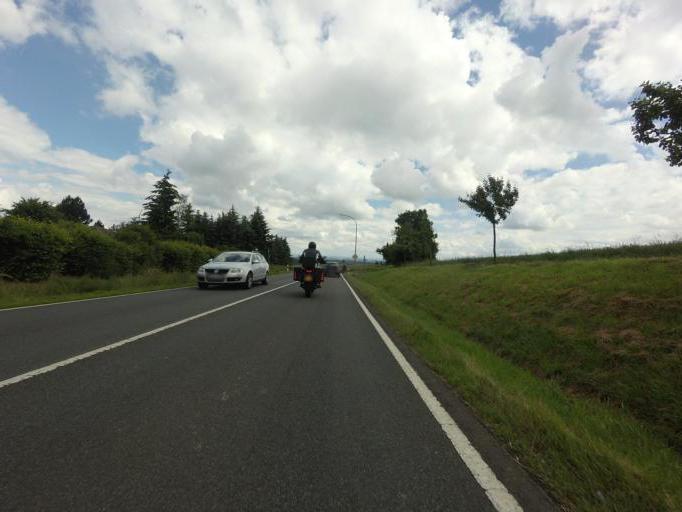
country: DE
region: Rheinland-Pfalz
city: Hirten
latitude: 50.3302
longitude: 7.1096
